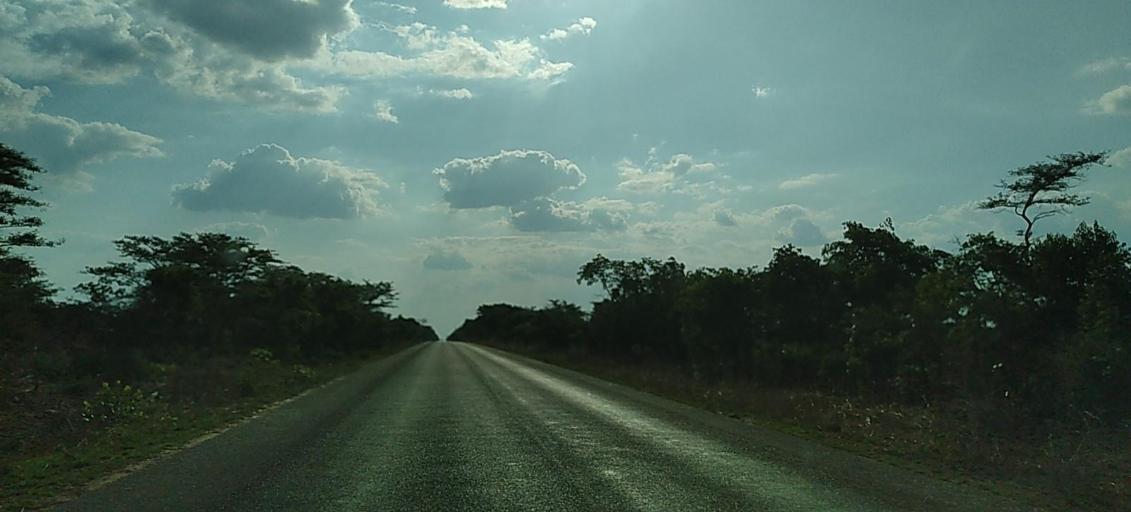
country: ZM
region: Copperbelt
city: Mpongwe
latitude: -13.3900
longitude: 28.3759
